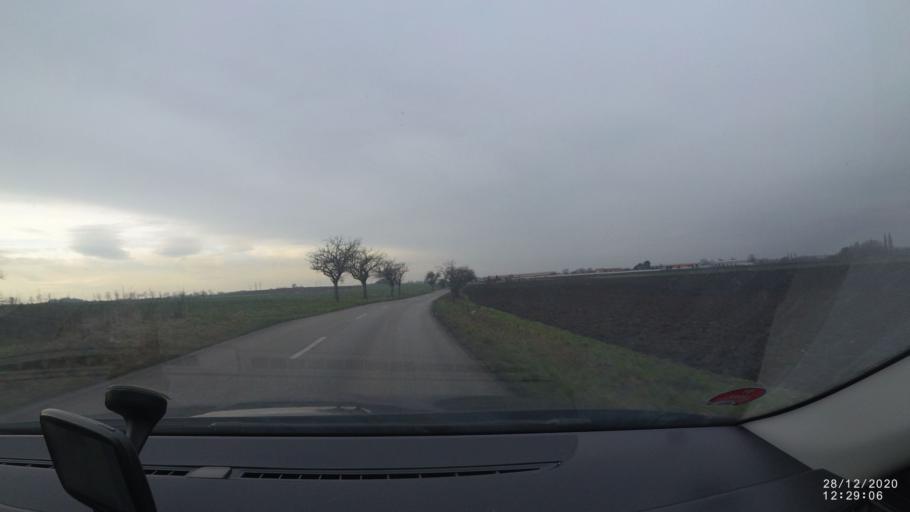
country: CZ
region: Central Bohemia
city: Brandys nad Labem-Stara Boleslav
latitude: 50.1964
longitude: 14.6204
